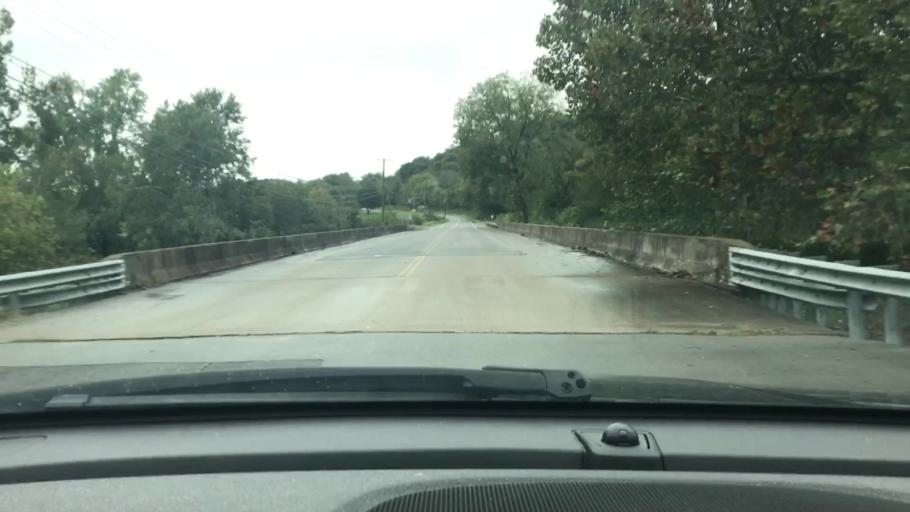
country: US
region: Tennessee
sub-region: Cheatham County
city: Kingston Springs
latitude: 36.1009
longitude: -87.1257
